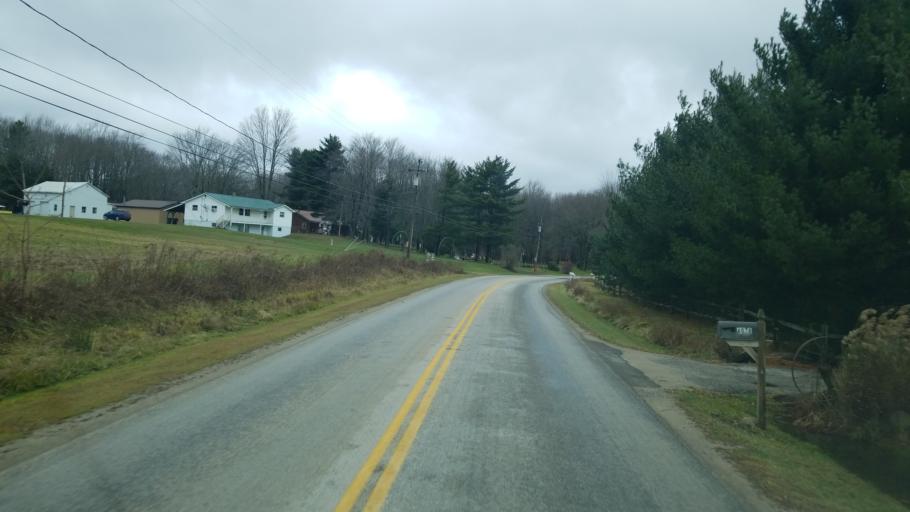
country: US
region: Ohio
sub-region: Ashtabula County
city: North Kingsville
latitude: 41.8373
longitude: -80.6223
